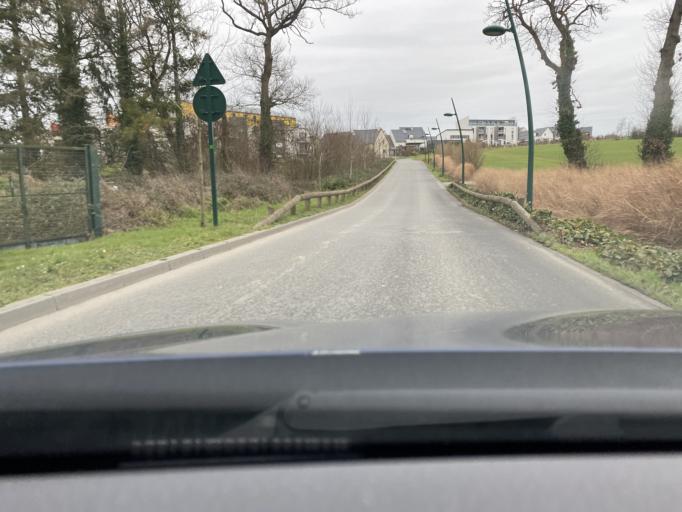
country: FR
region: Brittany
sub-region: Departement d'Ille-et-Vilaine
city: Melesse
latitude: 48.2128
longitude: -1.6953
